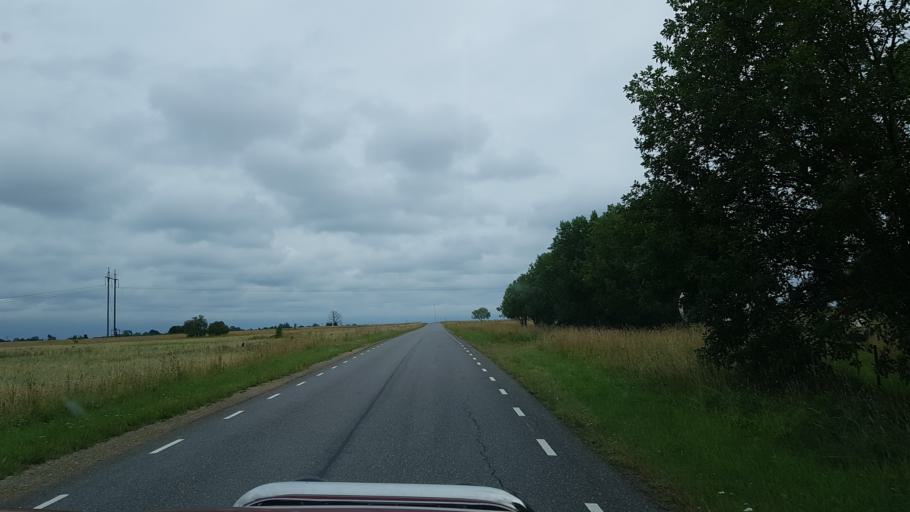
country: EE
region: Ida-Virumaa
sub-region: Puessi linn
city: Pussi
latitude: 59.3959
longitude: 27.0178
